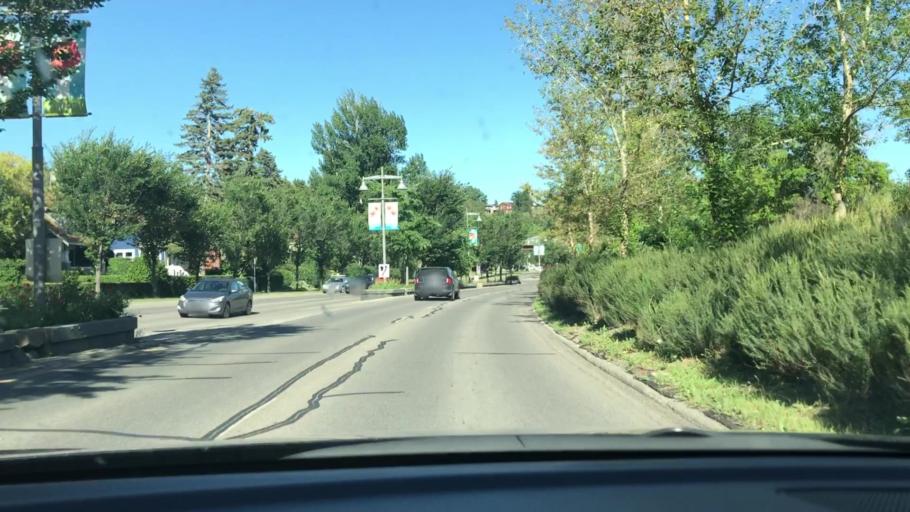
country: CA
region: Alberta
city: Calgary
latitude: 51.0575
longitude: -114.0719
